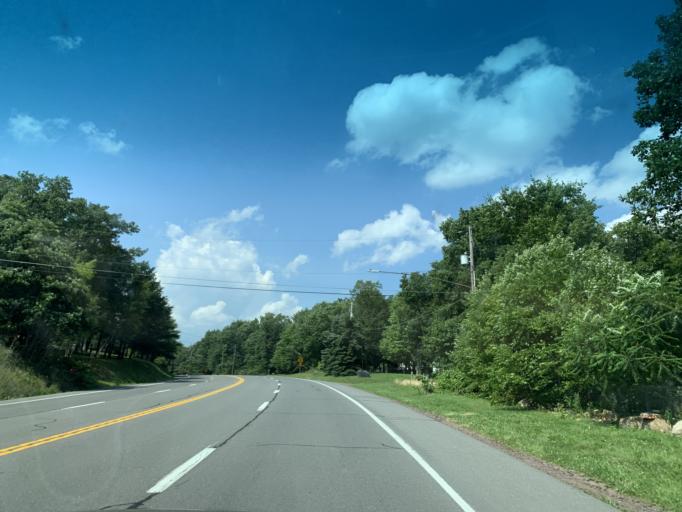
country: US
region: Pennsylvania
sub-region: Schuylkill County
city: Ashland
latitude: 40.8117
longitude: -76.3331
